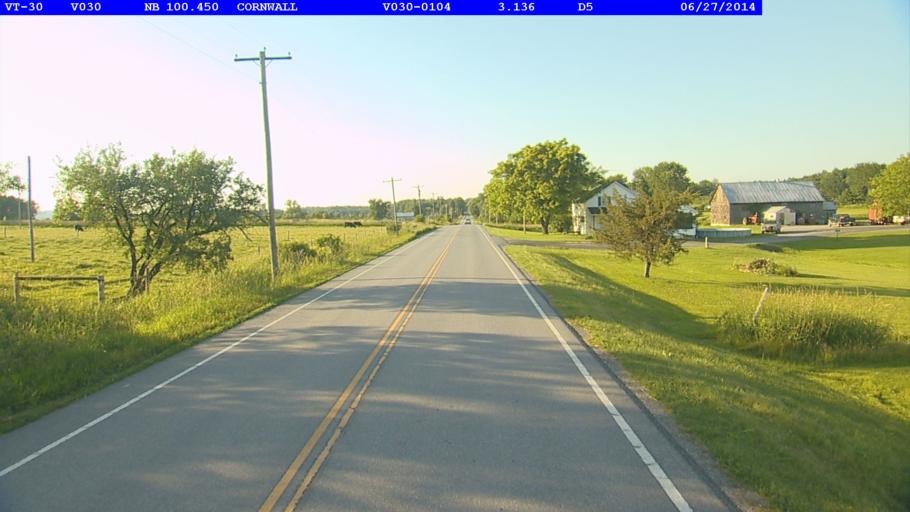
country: US
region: Vermont
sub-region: Addison County
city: Middlebury (village)
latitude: 43.9529
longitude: -73.2101
